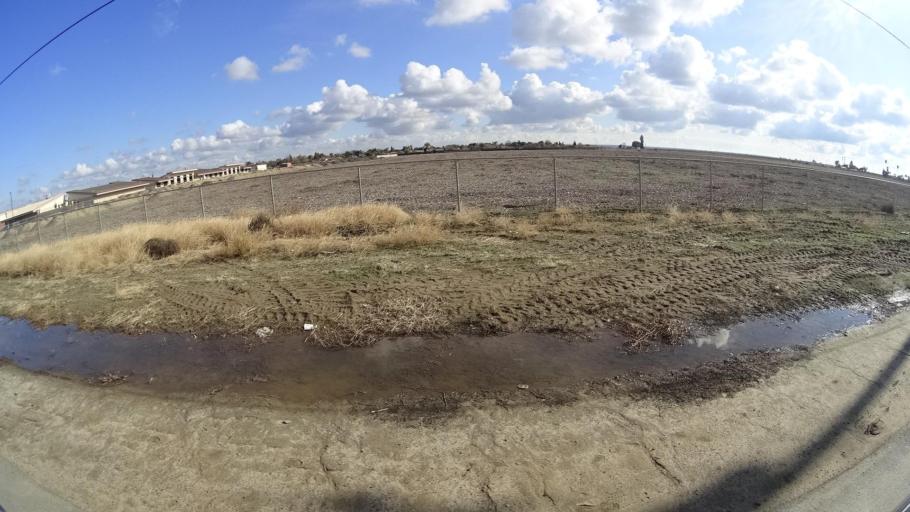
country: US
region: California
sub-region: Kern County
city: McFarland
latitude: 35.6647
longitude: -119.2410
